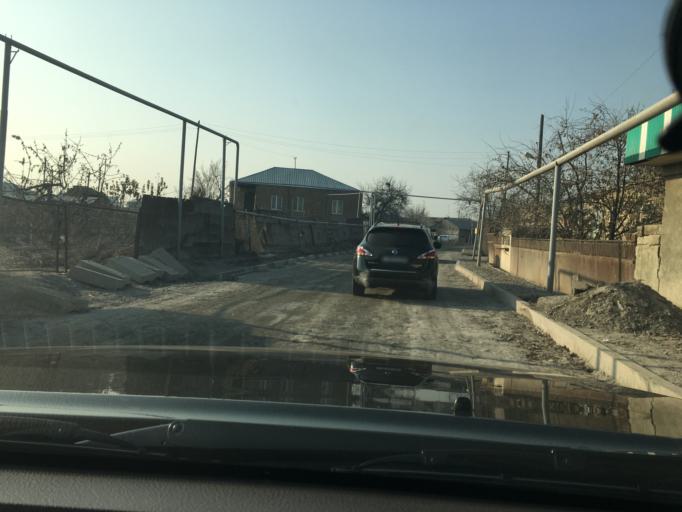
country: AM
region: Armavir
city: Janfida
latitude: 40.0448
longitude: 44.0290
